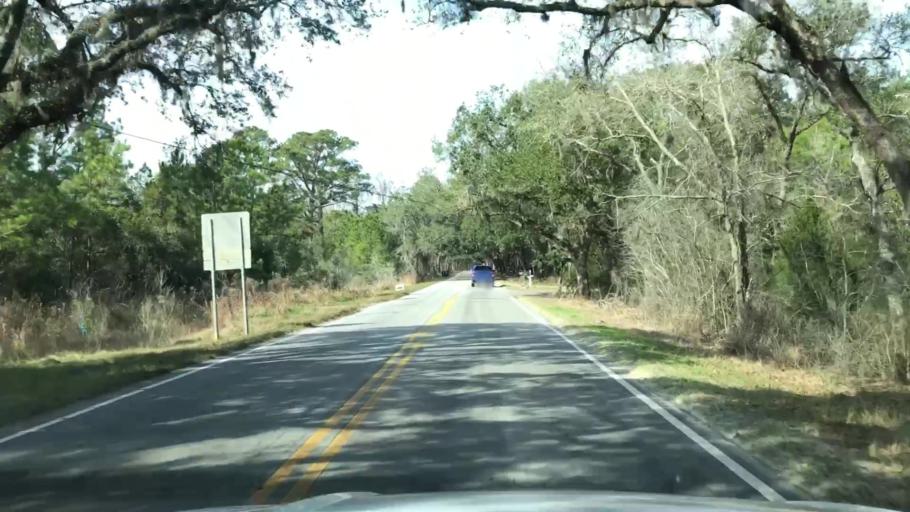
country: US
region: South Carolina
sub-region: Charleston County
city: Shell Point
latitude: 32.7548
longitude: -80.0488
